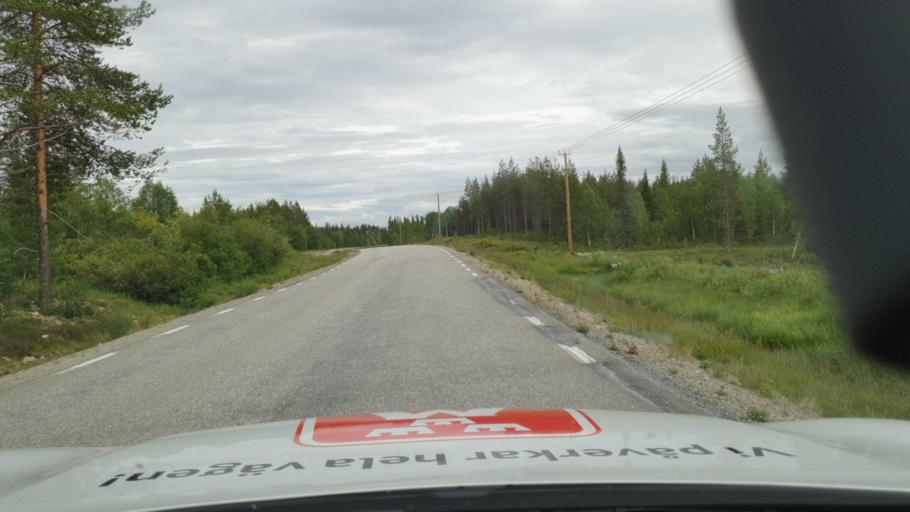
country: SE
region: Vaesterbotten
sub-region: Lycksele Kommun
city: Soderfors
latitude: 64.3733
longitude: 18.0555
